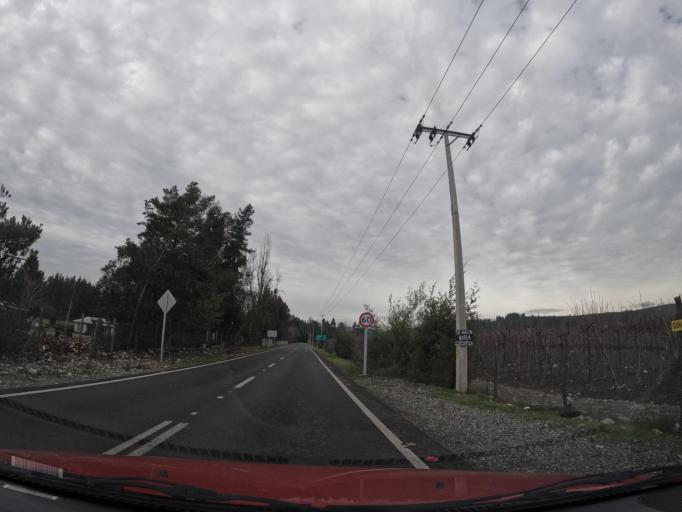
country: CL
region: Maule
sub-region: Provincia de Linares
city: Linares
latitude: -35.9125
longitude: -71.4924
